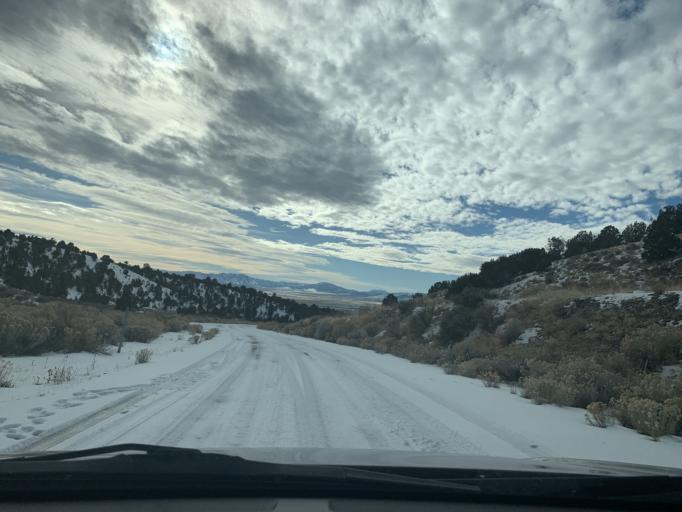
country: US
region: Utah
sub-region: Tooele County
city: Tooele
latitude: 40.3091
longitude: -112.2533
